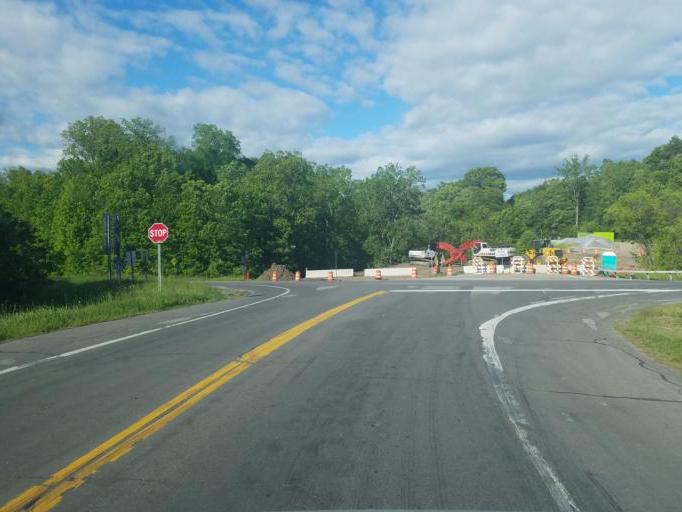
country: US
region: New York
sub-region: Herkimer County
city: Little Falls
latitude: 43.0253
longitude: -74.8210
